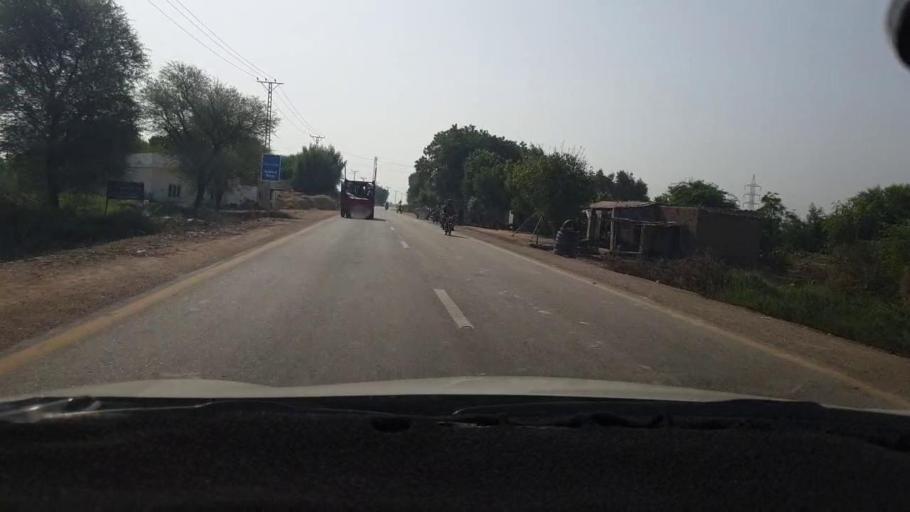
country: PK
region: Sindh
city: Jhol
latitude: 25.9432
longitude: 68.9855
